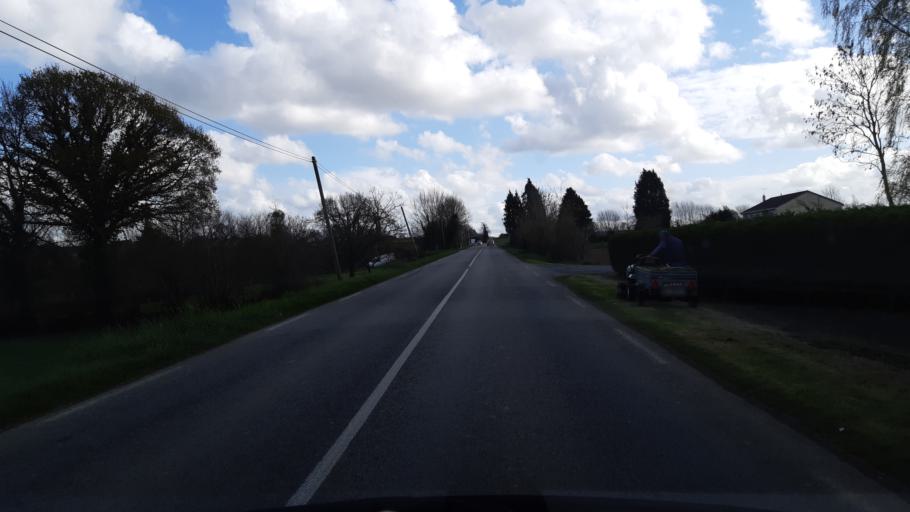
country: FR
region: Lower Normandy
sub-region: Departement de la Manche
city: Agneaux
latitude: 49.0578
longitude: -1.1331
